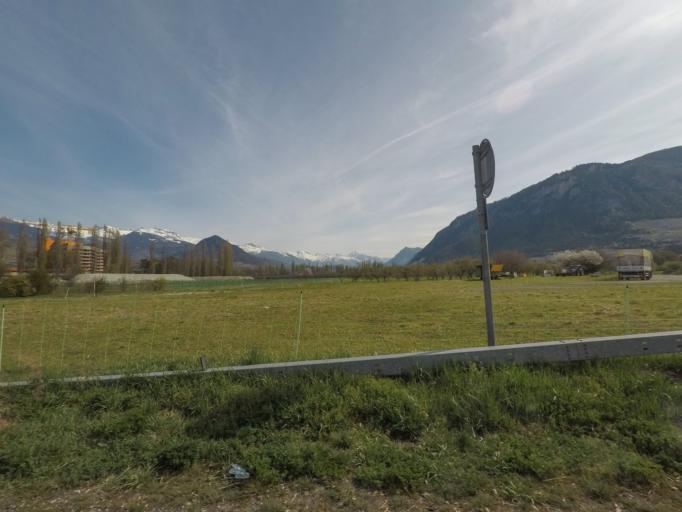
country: CH
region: Valais
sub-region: Herens District
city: Vex
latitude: 46.2312
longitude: 7.3852
